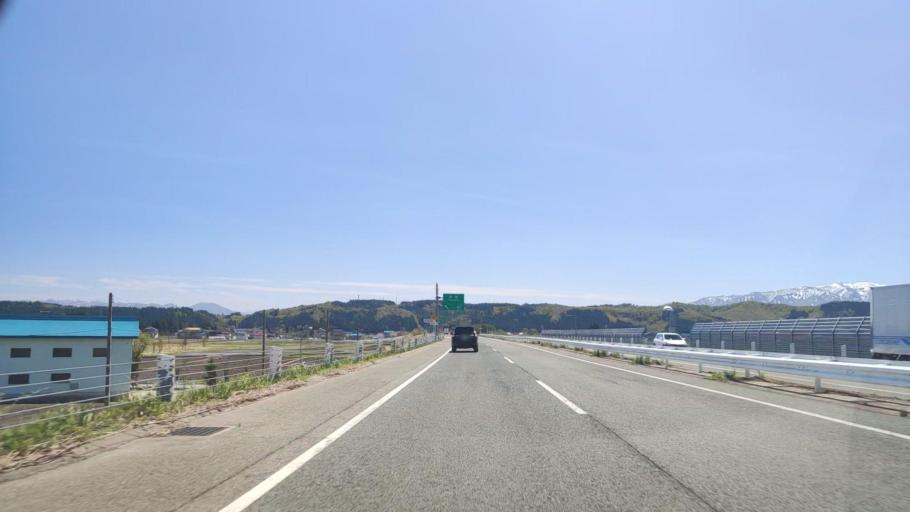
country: JP
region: Yamagata
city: Shinjo
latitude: 38.7079
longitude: 140.3088
